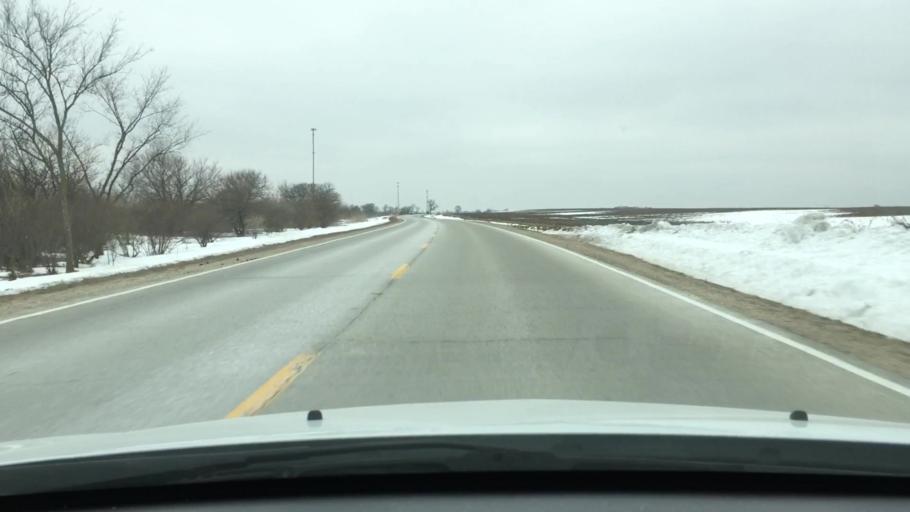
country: US
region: Illinois
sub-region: DeKalb County
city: Waterman
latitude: 41.7698
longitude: -88.7952
